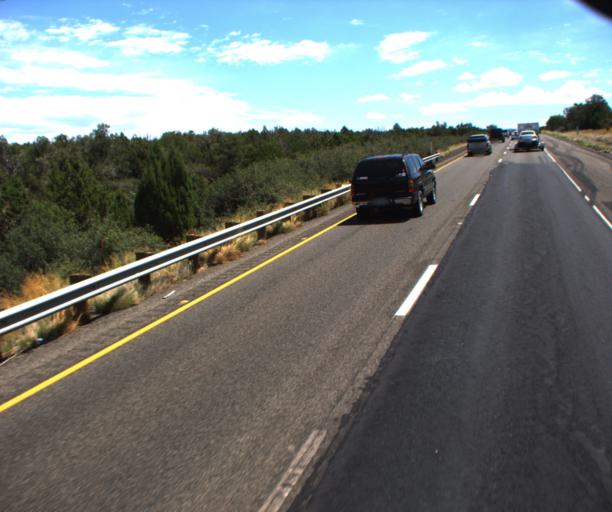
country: US
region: Arizona
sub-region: Yavapai County
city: Village of Oak Creek (Big Park)
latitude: 34.7746
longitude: -111.6324
